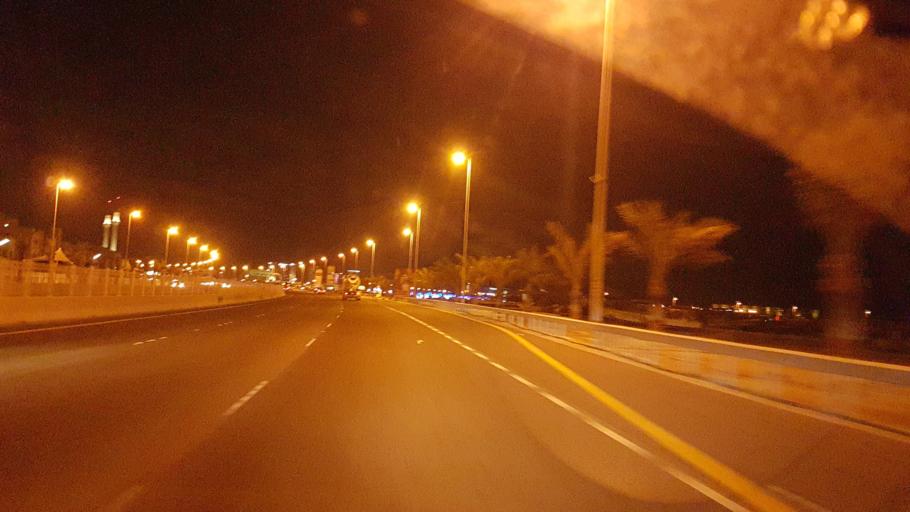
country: BH
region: Muharraq
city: Al Hadd
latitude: 26.2674
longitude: 50.6620
